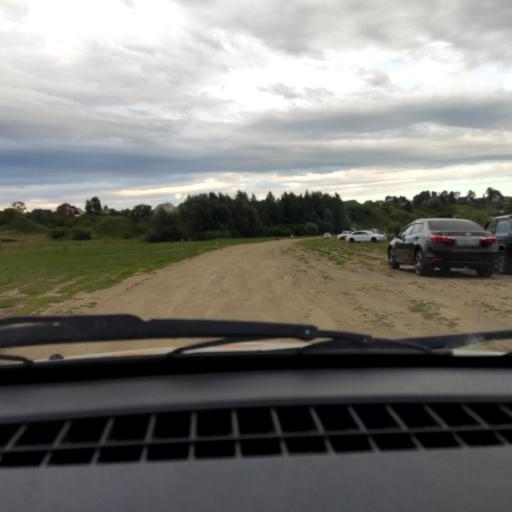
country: RU
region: Bashkortostan
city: Iglino
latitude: 54.7976
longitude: 56.2299
